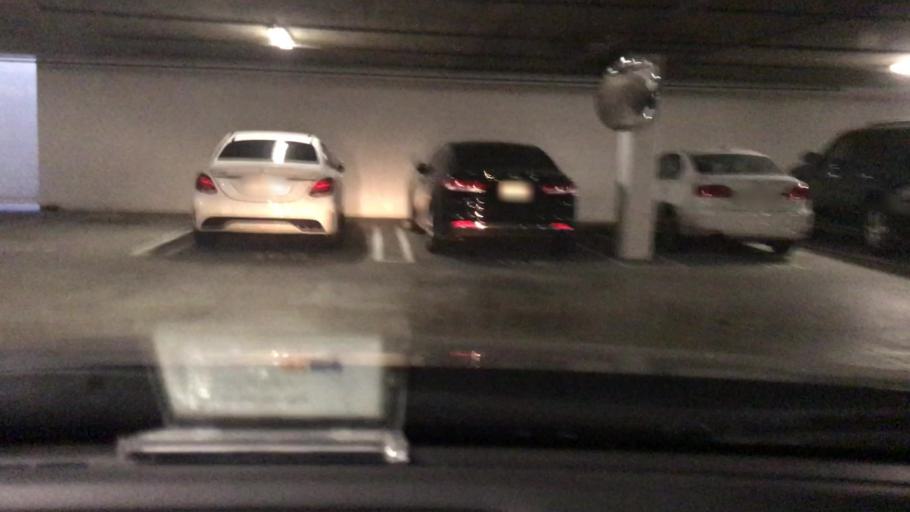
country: US
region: California
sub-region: Orange County
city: Laguna Woods
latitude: 33.6546
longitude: -117.7501
